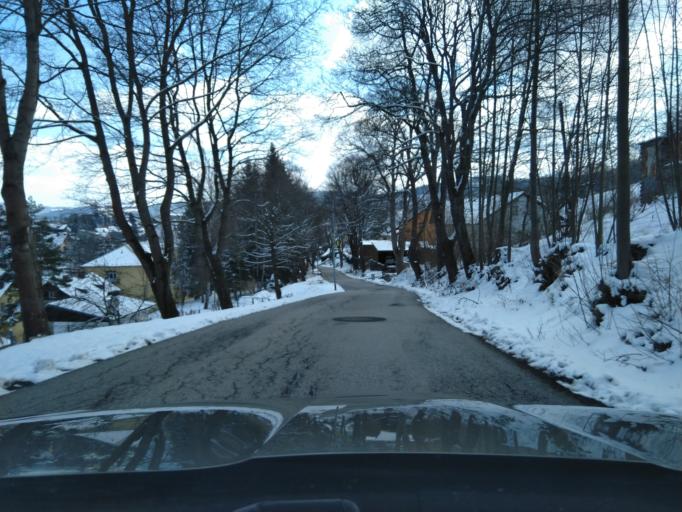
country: CZ
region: Jihocesky
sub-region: Okres Prachatice
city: Vimperk
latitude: 49.0572
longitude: 13.7620
